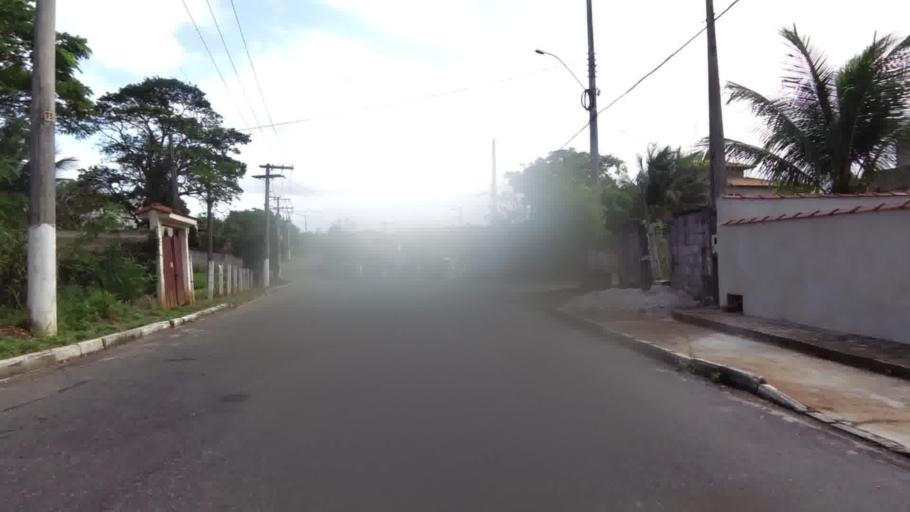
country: BR
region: Espirito Santo
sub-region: Piuma
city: Piuma
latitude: -20.8083
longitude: -40.6567
